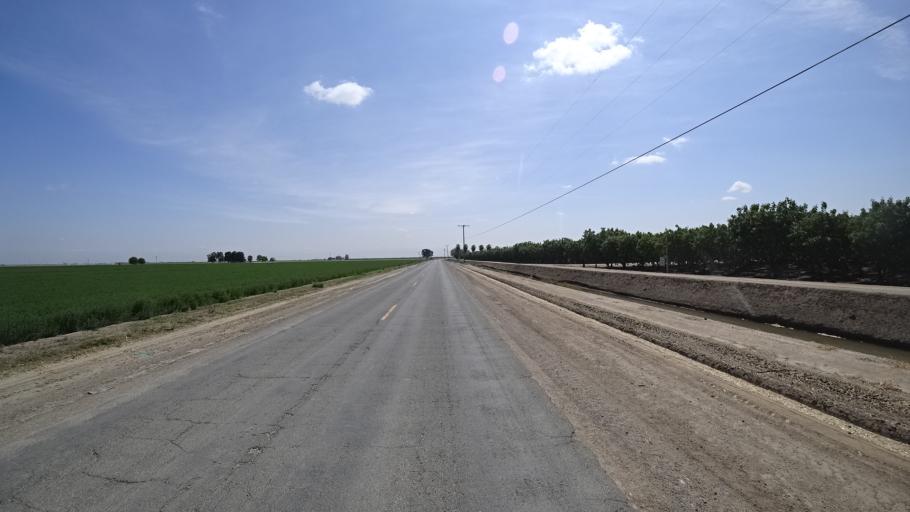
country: US
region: California
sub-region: Kings County
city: Home Garden
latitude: 36.2698
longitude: -119.5349
